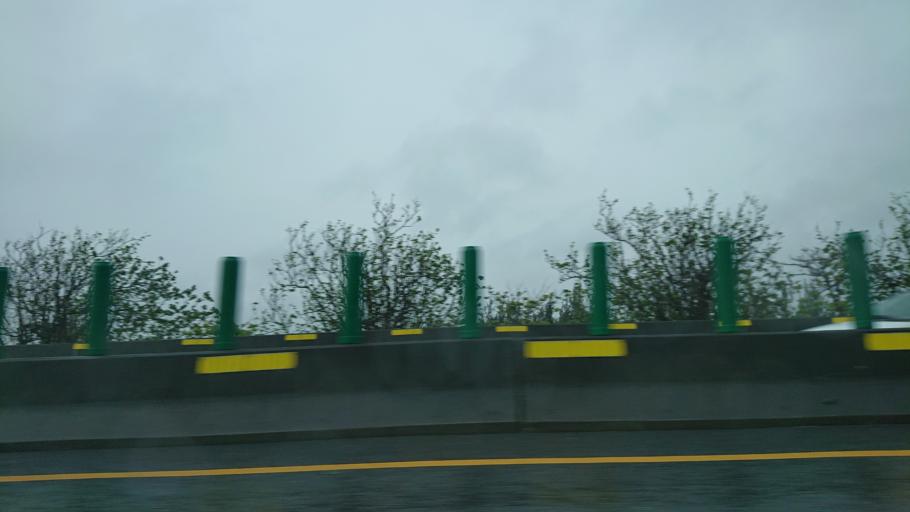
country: TW
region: Taiwan
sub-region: Chiayi
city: Taibao
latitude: 23.7185
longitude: 120.2138
